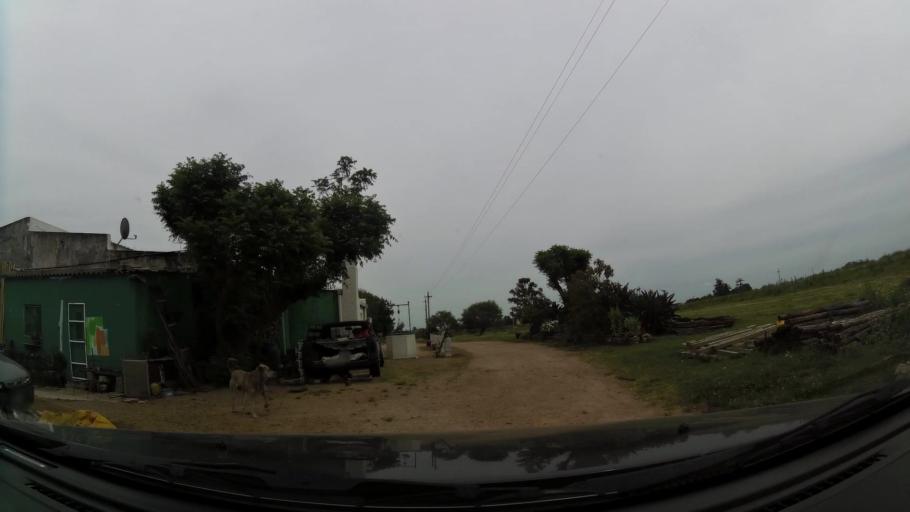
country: UY
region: Canelones
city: La Paz
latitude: -34.7450
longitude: -56.2394
